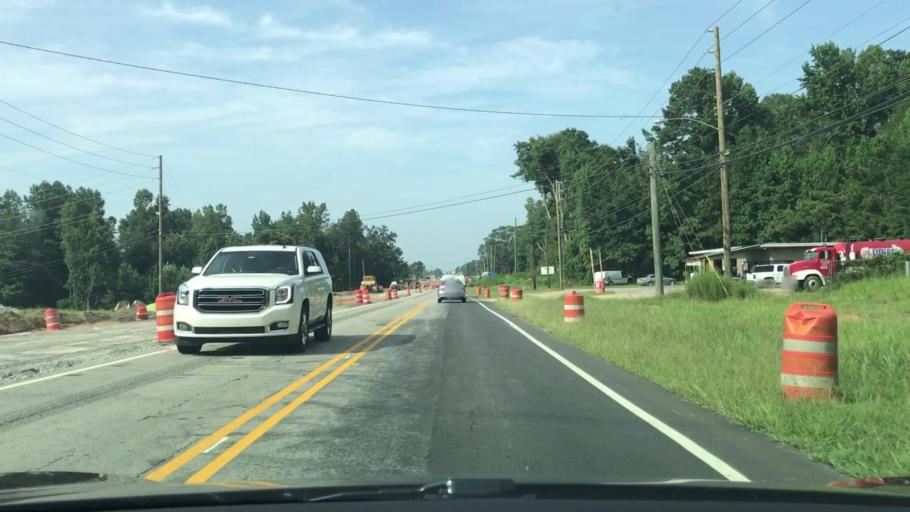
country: US
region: Georgia
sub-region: Gwinnett County
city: Buford
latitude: 34.1385
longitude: -83.9715
